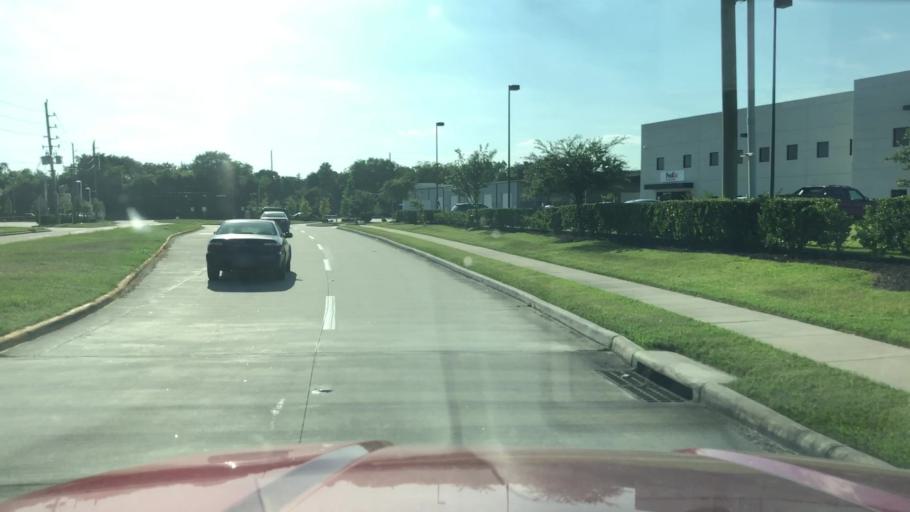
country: US
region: Texas
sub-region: Harris County
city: Hudson
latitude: 29.9463
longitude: -95.4960
